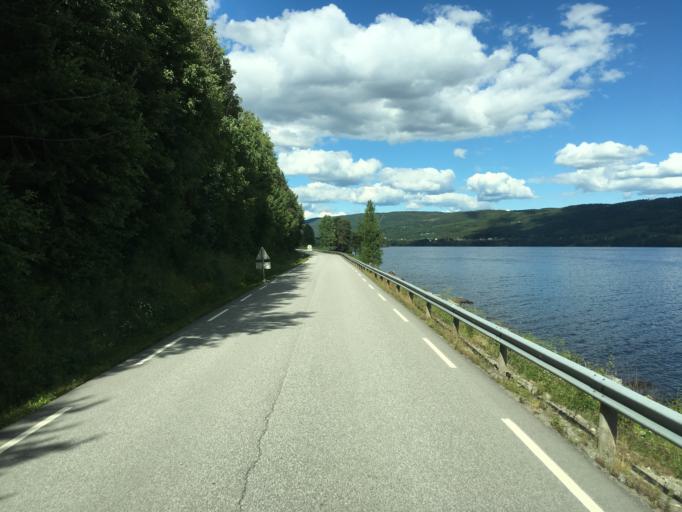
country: NO
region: Oppland
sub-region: Sondre Land
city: Hov
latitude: 60.6050
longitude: 10.3263
